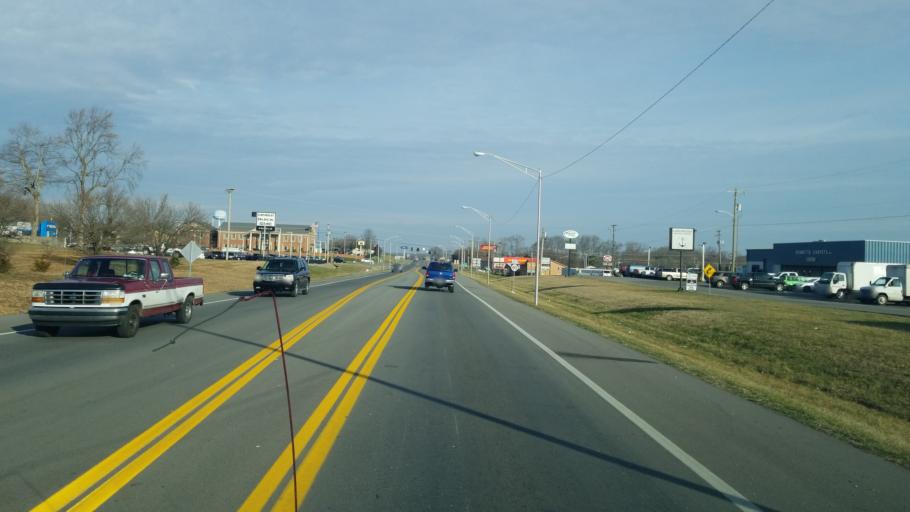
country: US
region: Kentucky
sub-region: Russell County
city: Russell Springs
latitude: 37.0637
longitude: -85.0709
